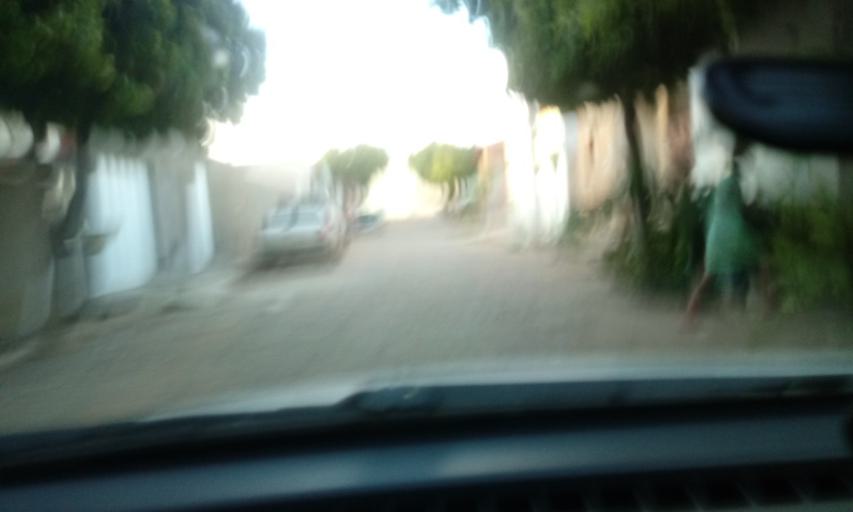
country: BR
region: Bahia
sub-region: Riacho De Santana
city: Riacho de Santana
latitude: -13.9083
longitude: -42.8464
